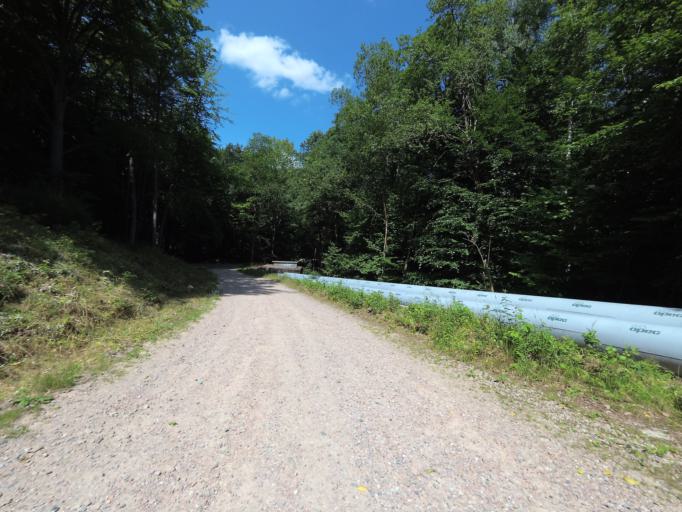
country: PL
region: Pomeranian Voivodeship
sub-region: Gdynia
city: Wielki Kack
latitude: 54.4878
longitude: 18.5025
